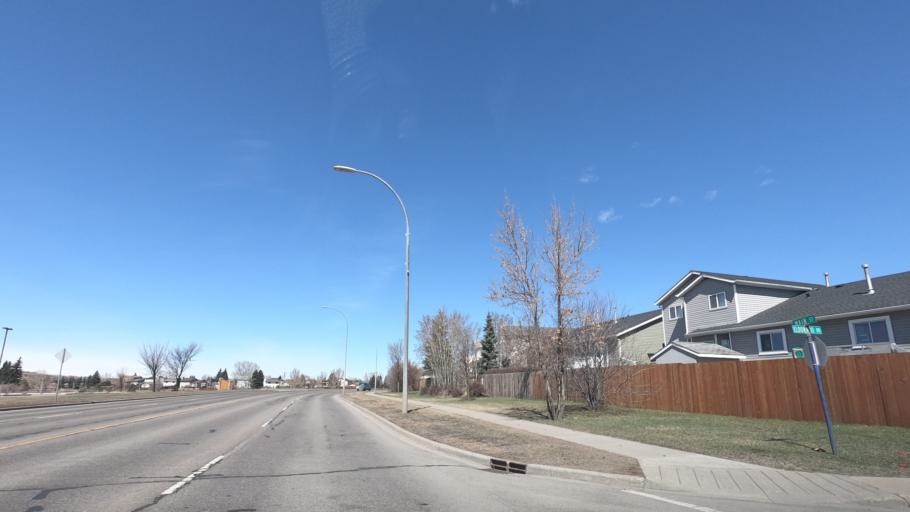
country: CA
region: Alberta
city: Airdrie
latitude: 51.2814
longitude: -114.0100
